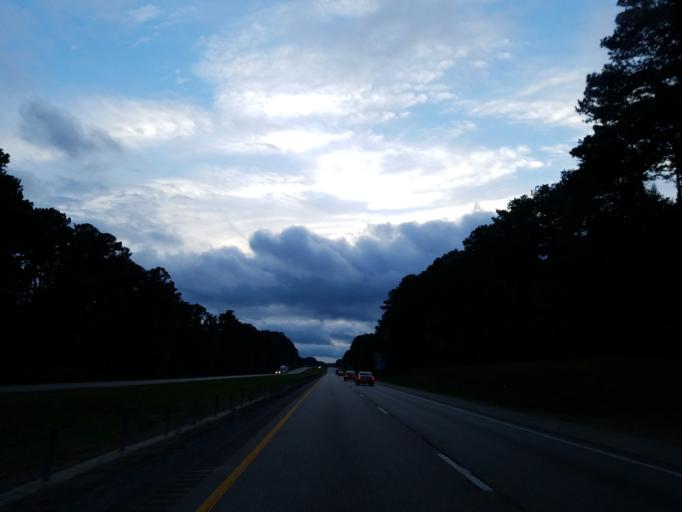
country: US
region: Mississippi
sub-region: Lauderdale County
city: Marion
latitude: 32.3991
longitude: -88.5692
